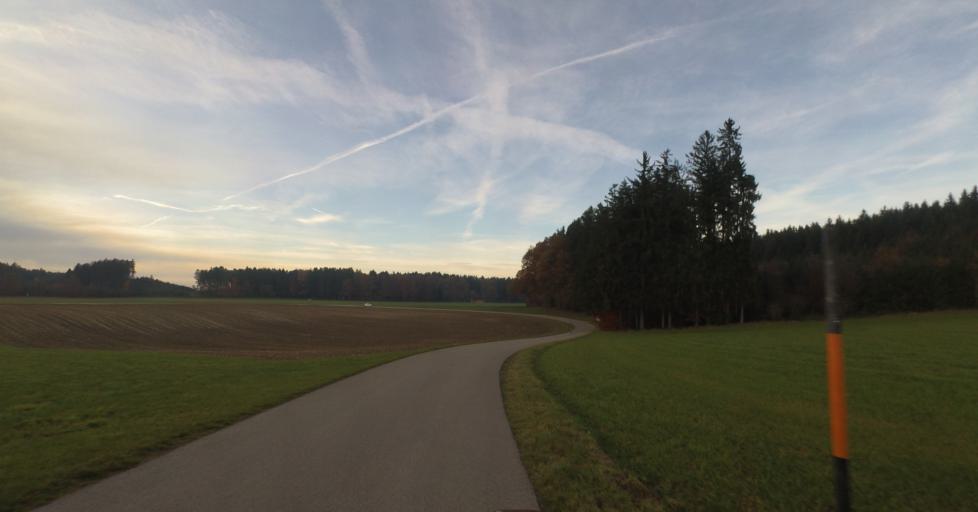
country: DE
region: Bavaria
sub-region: Upper Bavaria
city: Nussdorf
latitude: 47.8948
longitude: 12.5942
